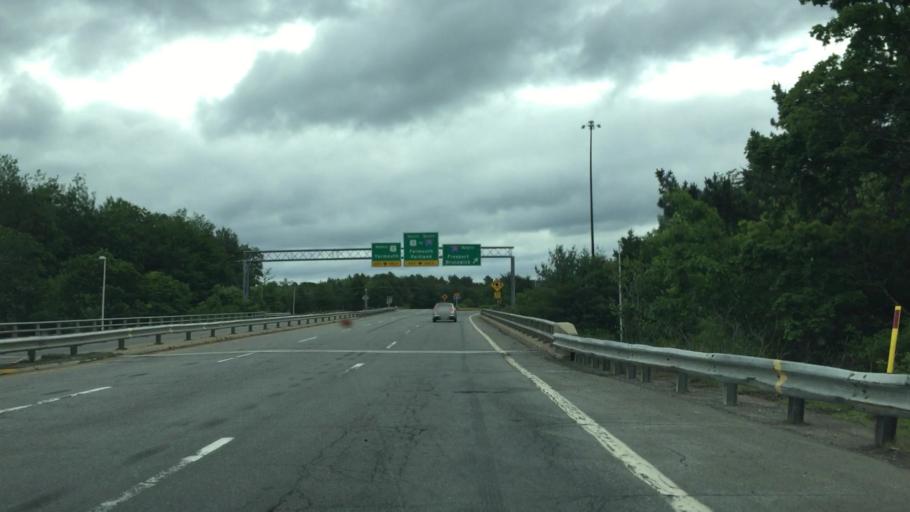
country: US
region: Maine
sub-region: Cumberland County
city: Falmouth
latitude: 43.7315
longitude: -70.2320
